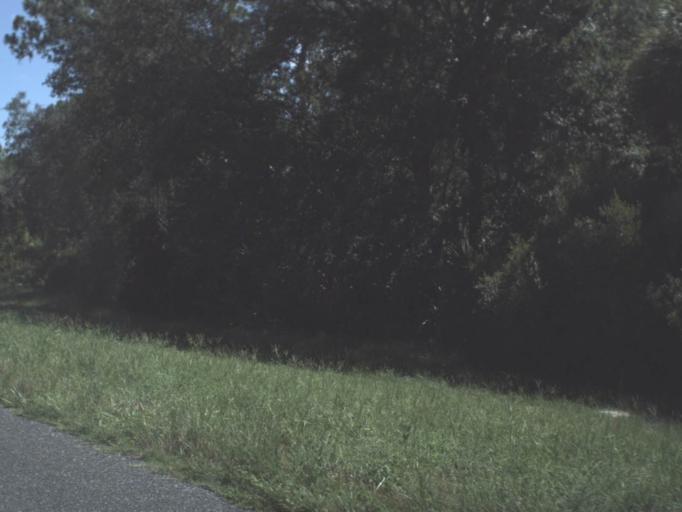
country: US
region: Florida
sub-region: Levy County
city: Inglis
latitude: 29.1313
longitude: -82.6368
